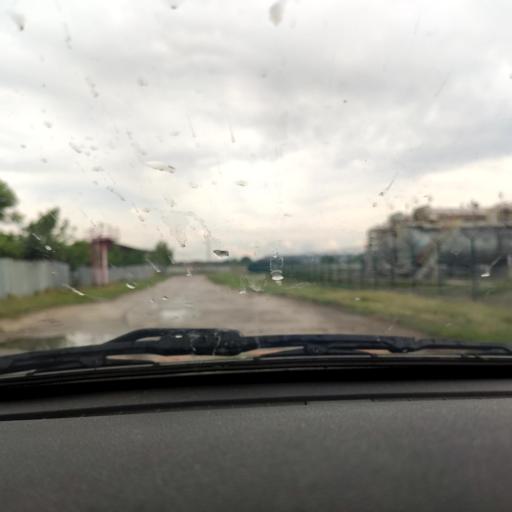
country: RU
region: Samara
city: Tol'yatti
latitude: 53.5350
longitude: 49.4679
